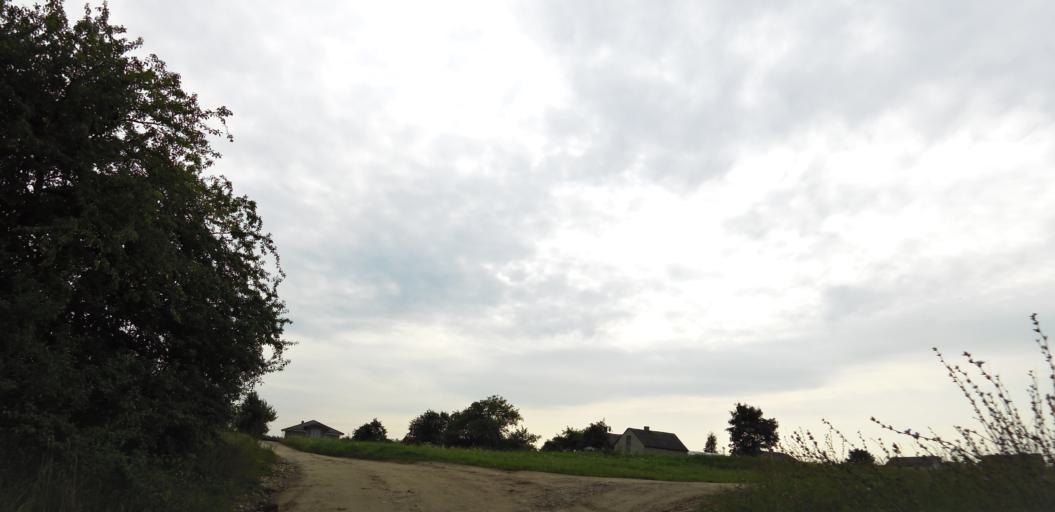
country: LT
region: Vilnius County
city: Pasilaiciai
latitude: 54.7610
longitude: 25.2282
